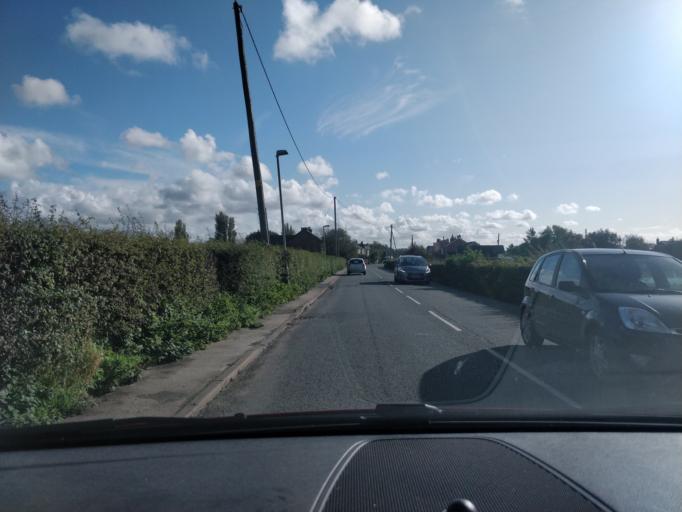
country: GB
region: England
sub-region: Lancashire
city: Banks
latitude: 53.6885
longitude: -2.9143
